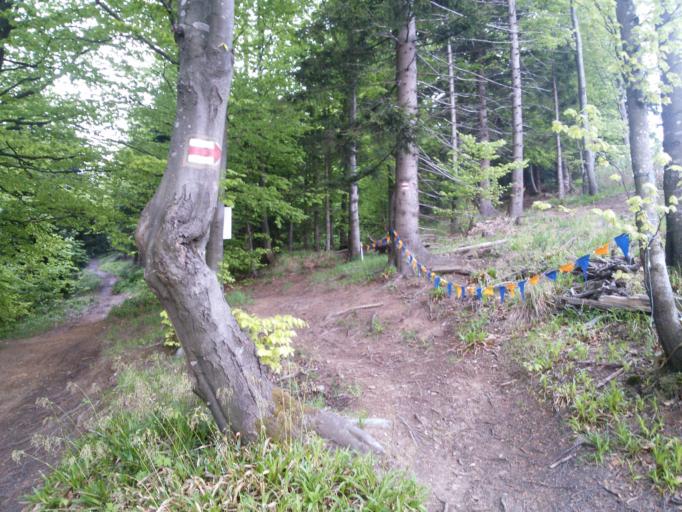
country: CZ
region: Olomoucky
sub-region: Okres Sumperk
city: Loucna nad Desnou
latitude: 50.0915
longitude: 17.1360
